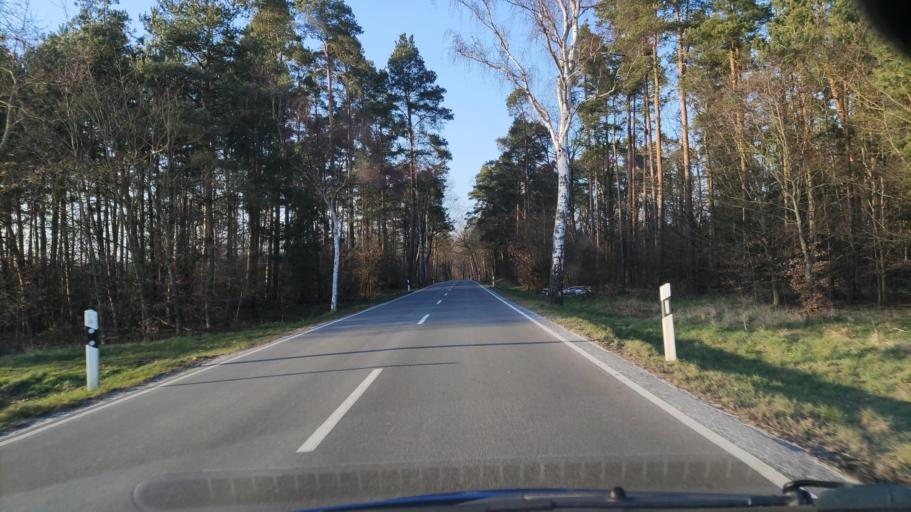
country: DE
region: Brandenburg
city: Lanz
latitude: 53.0117
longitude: 11.5484
